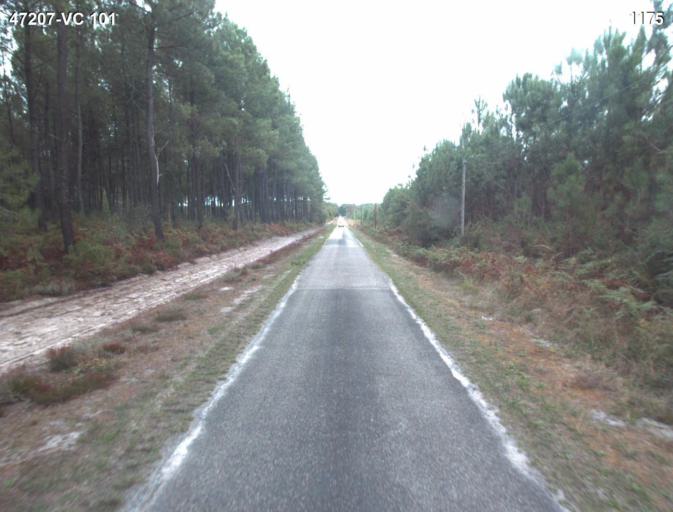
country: FR
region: Aquitaine
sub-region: Departement du Lot-et-Garonne
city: Barbaste
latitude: 44.1828
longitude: 0.1936
